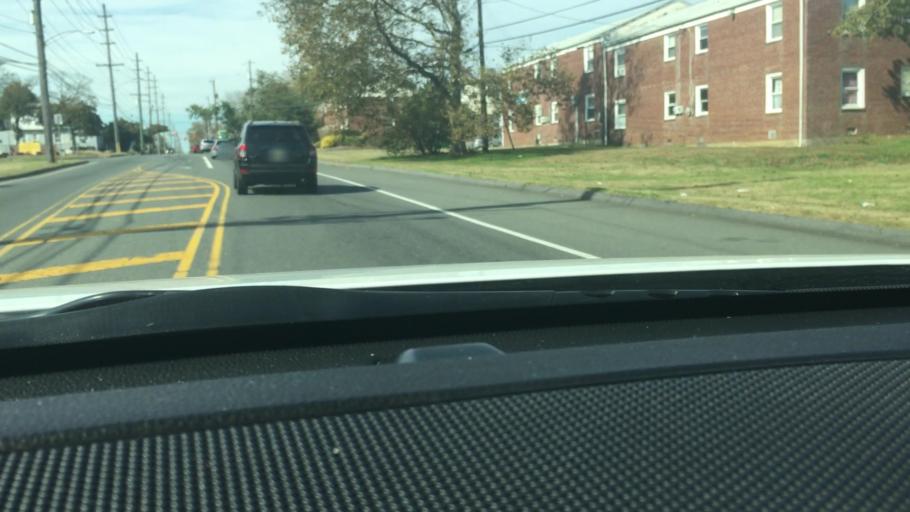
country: US
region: New Jersey
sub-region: Atlantic County
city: Pleasantville
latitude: 39.4030
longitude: -74.5087
